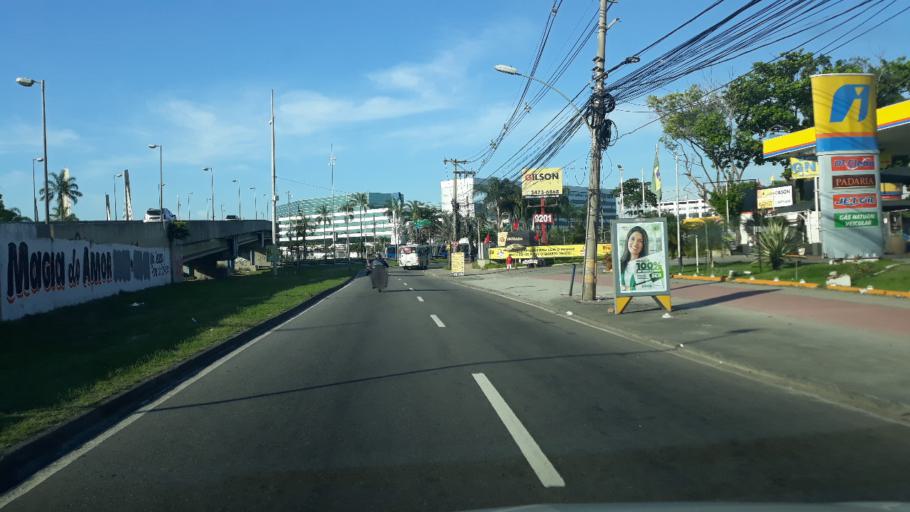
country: BR
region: Rio de Janeiro
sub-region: Sao Joao De Meriti
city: Sao Joao de Meriti
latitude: -22.9724
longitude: -43.3628
